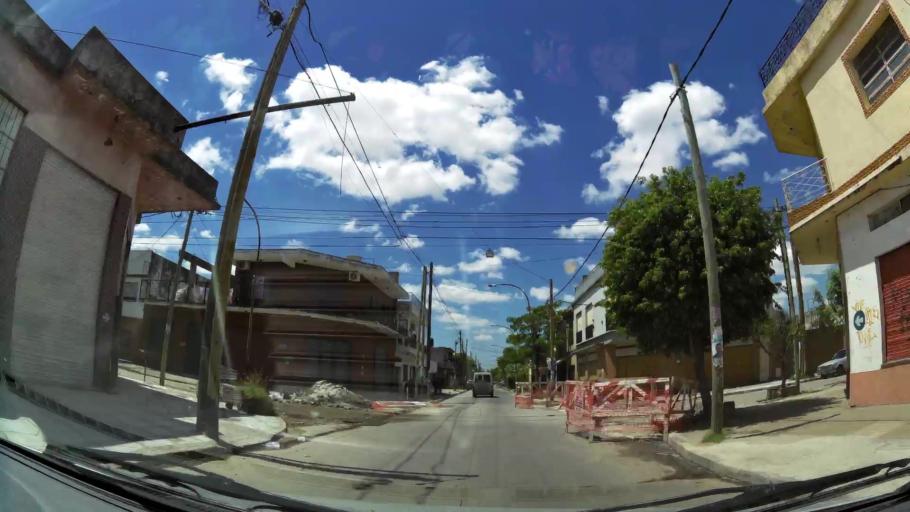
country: AR
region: Buenos Aires
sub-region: Partido de Lanus
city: Lanus
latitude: -34.7272
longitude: -58.4163
